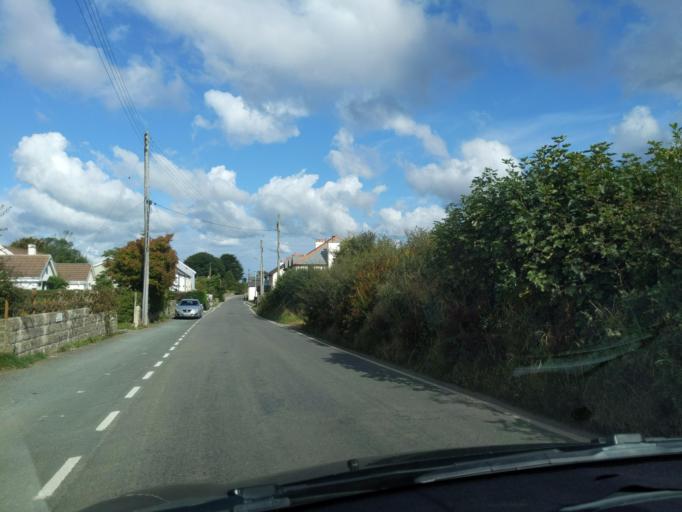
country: GB
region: England
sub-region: Devon
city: Great Torrington
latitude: 50.9183
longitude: -4.2113
